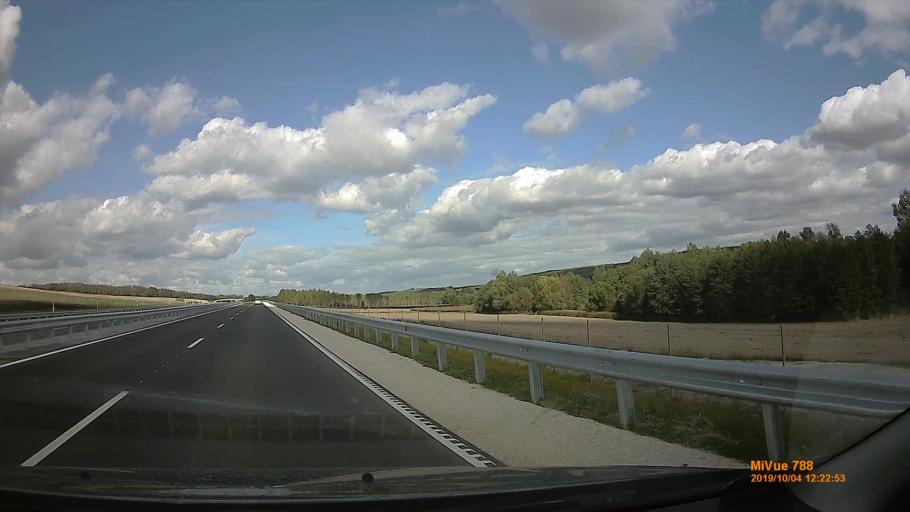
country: HU
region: Somogy
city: Karad
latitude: 46.6271
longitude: 17.7943
